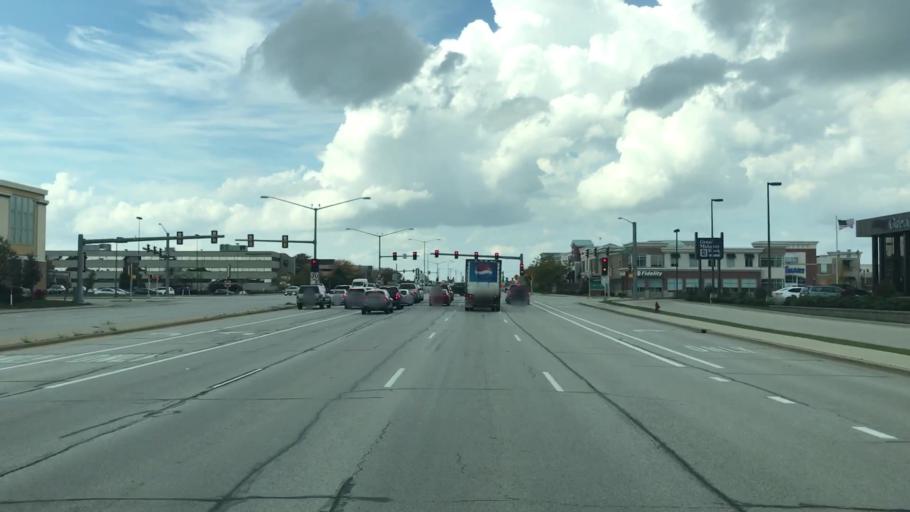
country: US
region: Wisconsin
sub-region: Waukesha County
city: Brookfield
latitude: 43.0362
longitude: -88.1102
